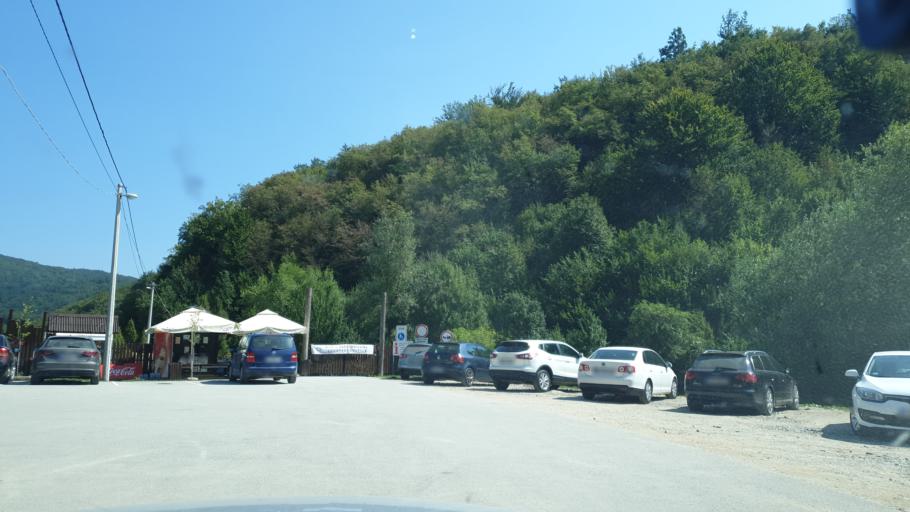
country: RS
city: Zlatibor
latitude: 43.6549
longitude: 19.8333
